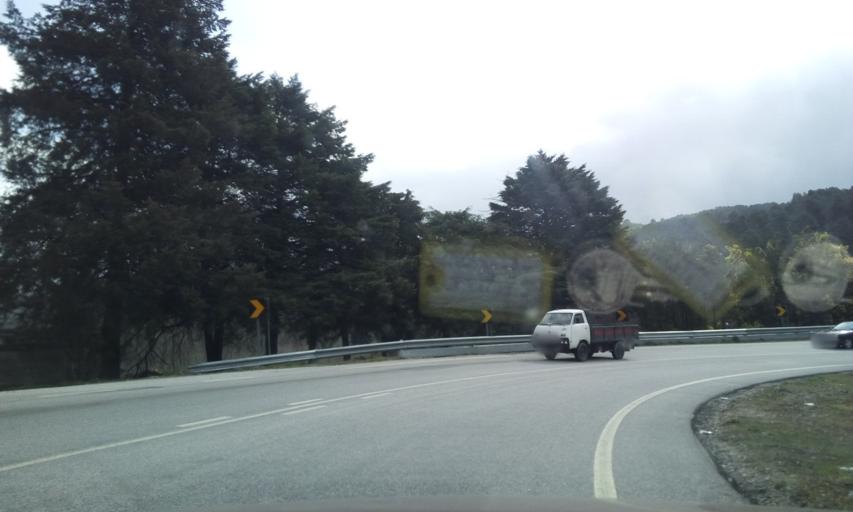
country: PT
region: Viseu
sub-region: Mangualde
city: Mangualde
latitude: 40.6476
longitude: -7.7296
